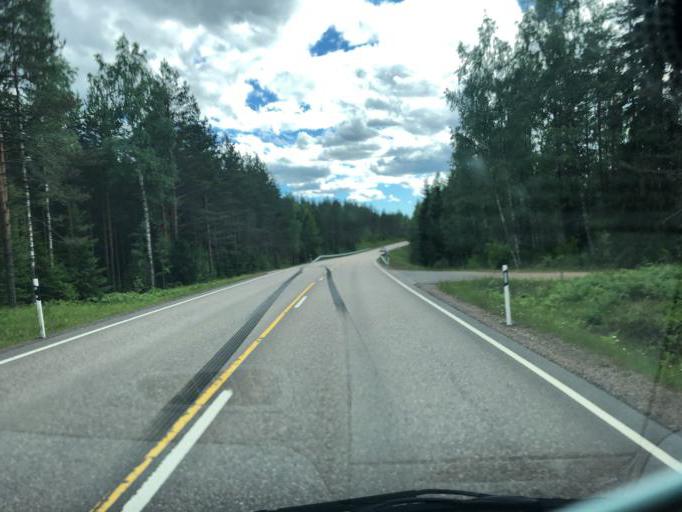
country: FI
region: Southern Savonia
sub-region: Mikkeli
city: Maentyharju
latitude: 61.1032
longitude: 27.1009
